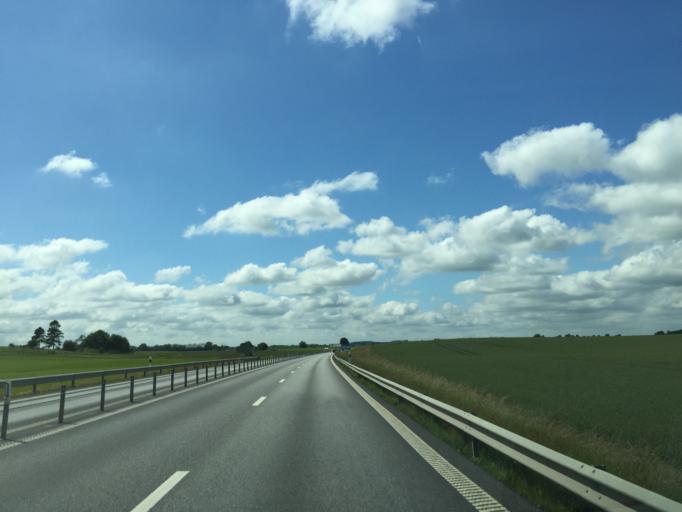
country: SE
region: Skane
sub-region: Skurups Kommun
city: Rydsgard
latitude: 55.4833
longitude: 13.5878
